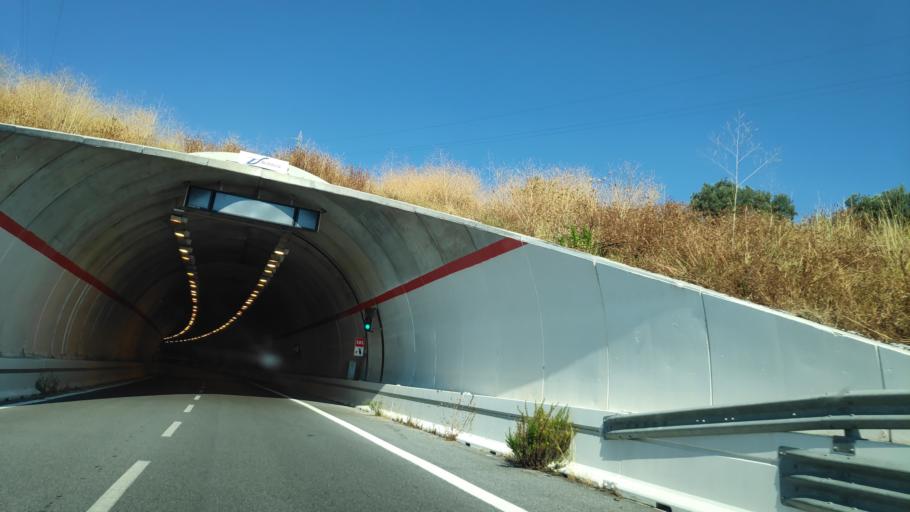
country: IT
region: Calabria
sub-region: Provincia di Reggio Calabria
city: Marina di Gioiosa Ionica
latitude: 38.3154
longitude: 16.3201
